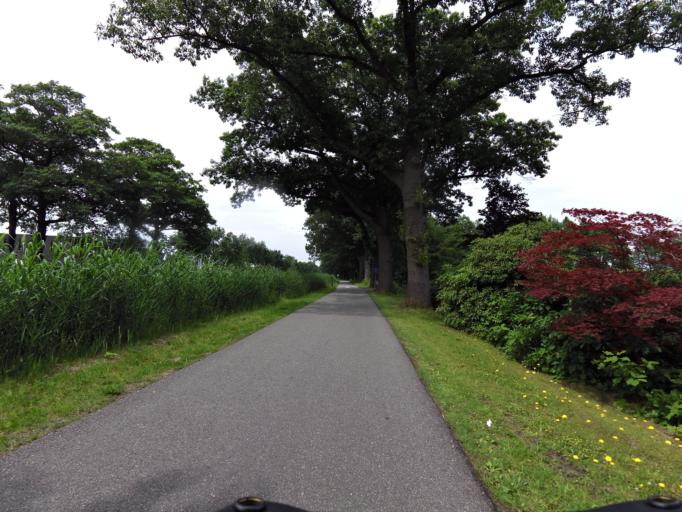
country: NL
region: Gelderland
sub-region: Gemeente Apeldoorn
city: Beekbergen
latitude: 52.1618
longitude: 6.0064
